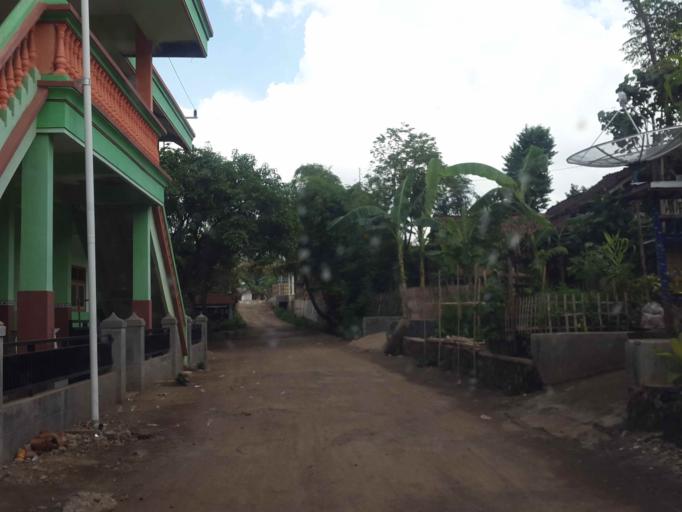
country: ID
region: East Java
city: Sukorejo
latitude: -7.9300
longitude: 113.9716
